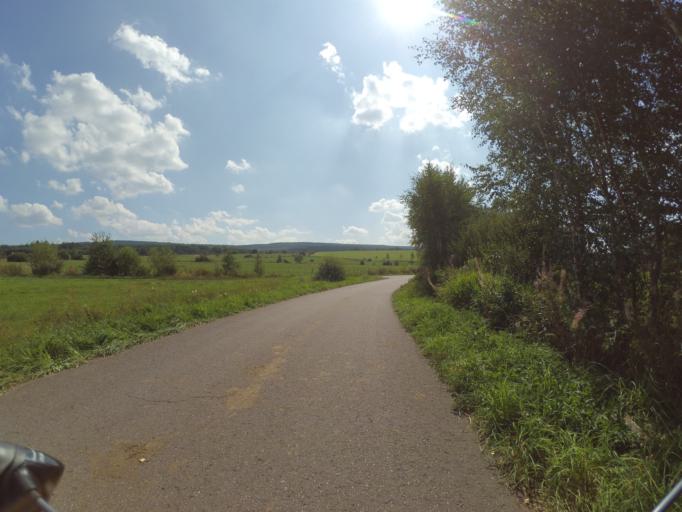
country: DE
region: Rheinland-Pfalz
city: Morbach
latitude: 49.8263
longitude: 7.1561
